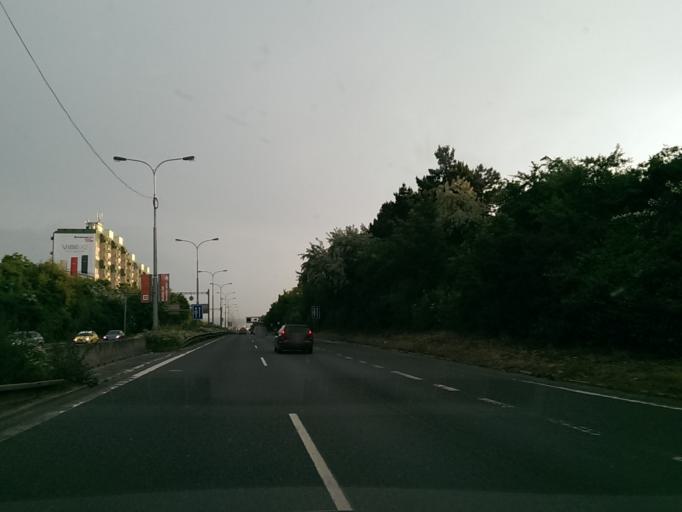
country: CZ
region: Praha
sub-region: Praha 9
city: Strizkov
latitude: 50.1283
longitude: 14.4853
